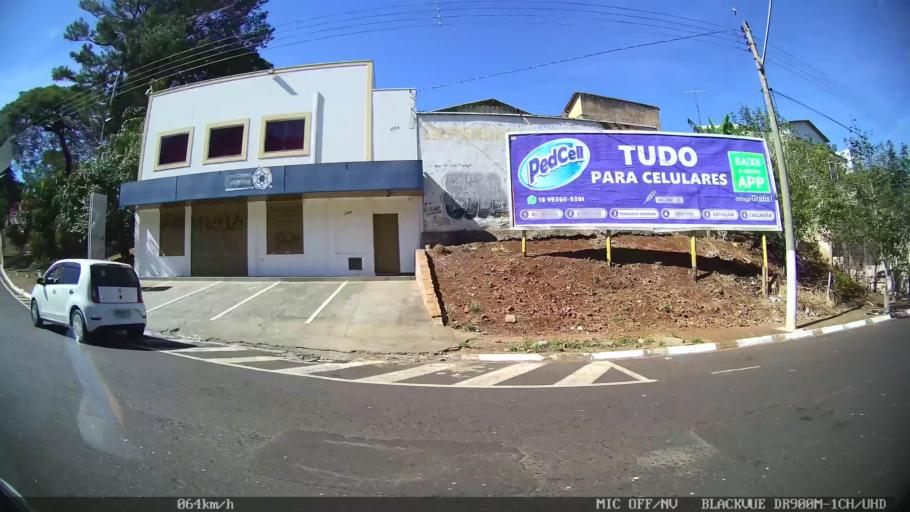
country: BR
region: Sao Paulo
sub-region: Franca
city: Franca
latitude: -20.5377
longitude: -47.4072
